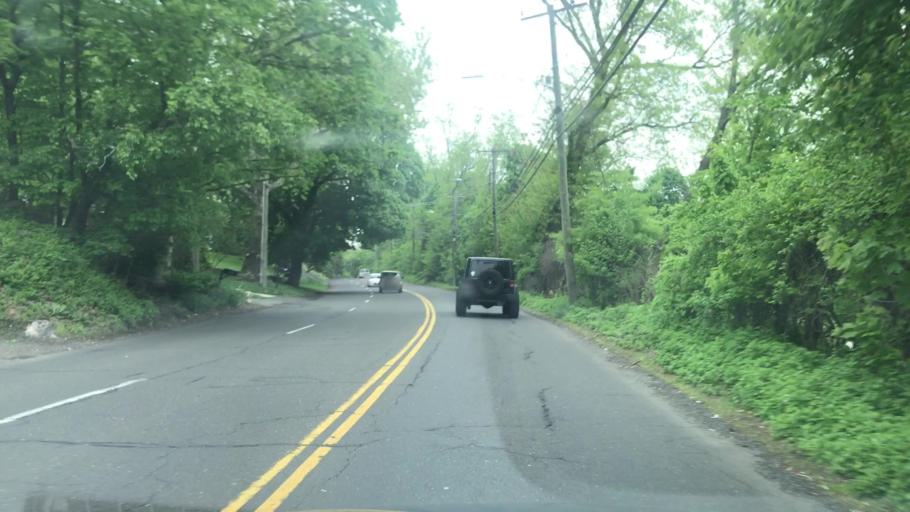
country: US
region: Connecticut
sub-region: Fairfield County
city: Stamford
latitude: 41.0605
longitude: -73.5593
